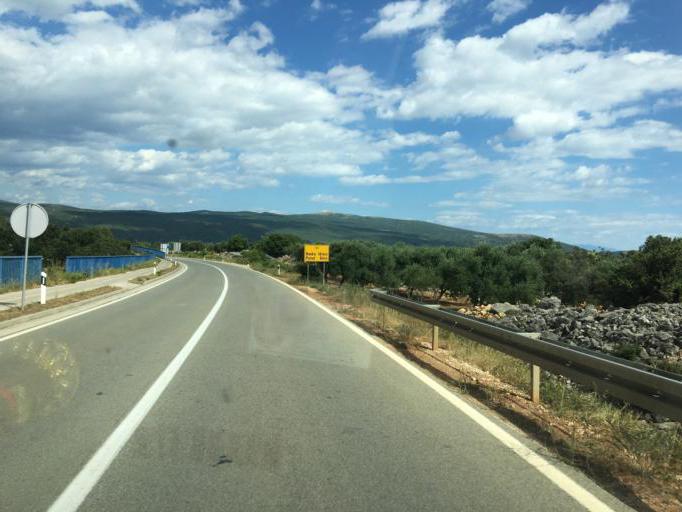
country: HR
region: Primorsko-Goranska
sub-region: Grad Krk
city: Krk
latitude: 45.0308
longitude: 14.5947
